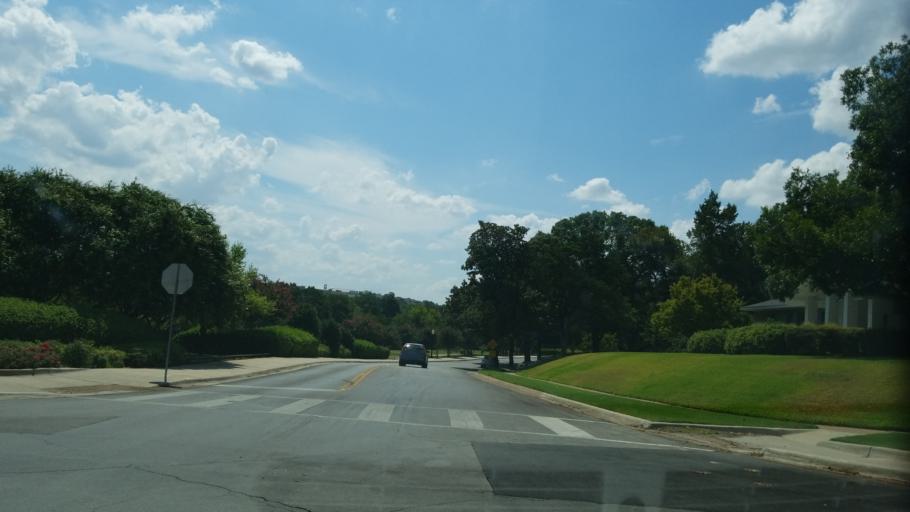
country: US
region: Texas
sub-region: Dallas County
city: Cockrell Hill
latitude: 32.7602
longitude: -96.8504
